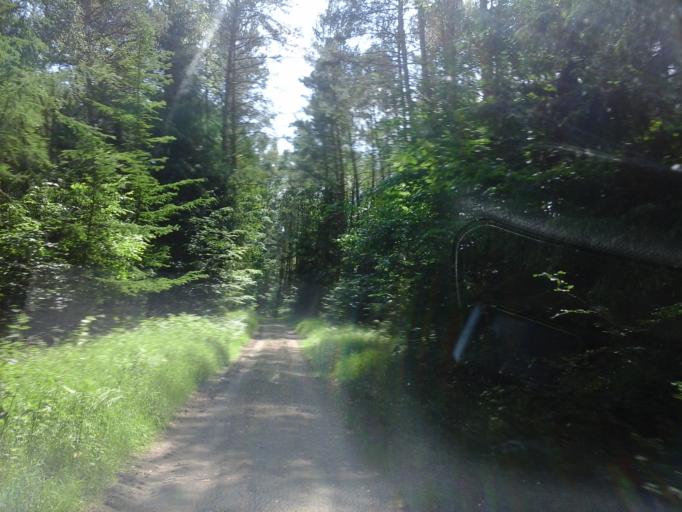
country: PL
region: West Pomeranian Voivodeship
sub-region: Powiat choszczenski
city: Bierzwnik
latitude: 53.0753
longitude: 15.6644
